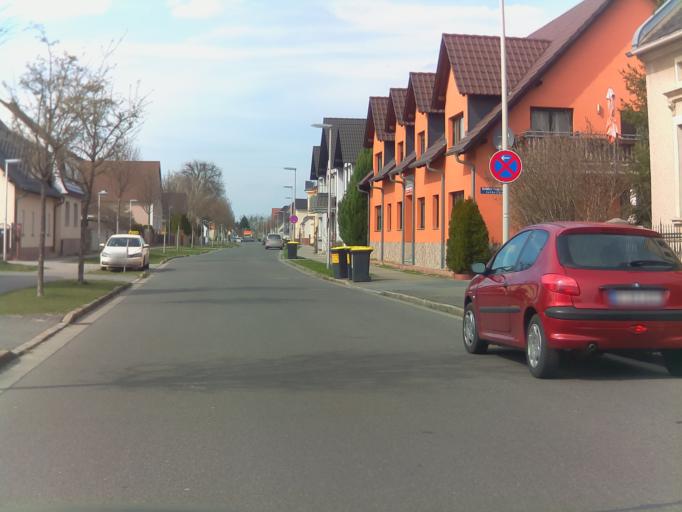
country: DE
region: Brandenburg
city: Cottbus
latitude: 51.7552
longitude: 14.3023
